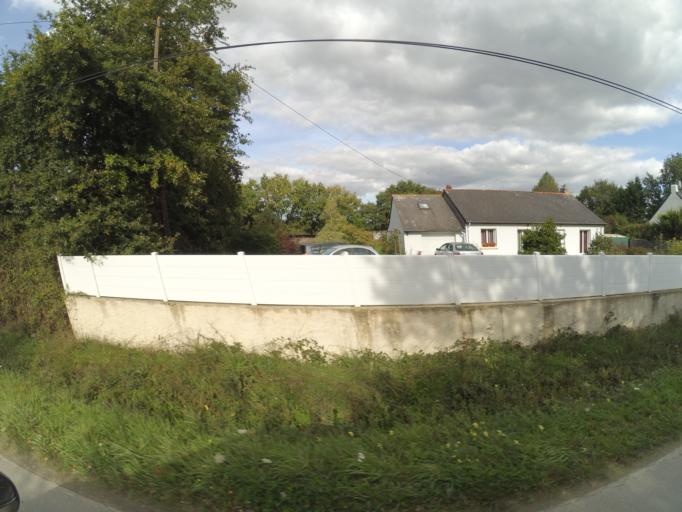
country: FR
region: Pays de la Loire
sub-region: Departement de la Loire-Atlantique
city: Casson
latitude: 47.3988
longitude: -1.5697
